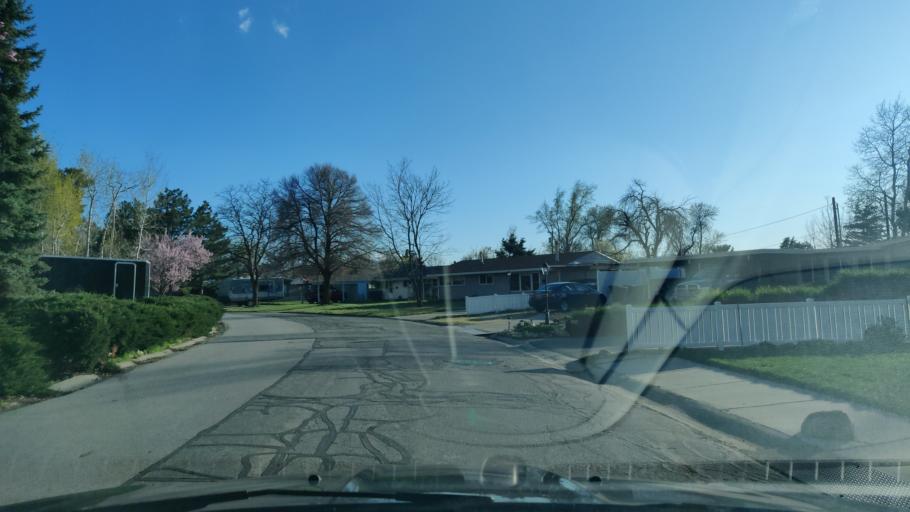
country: US
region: Utah
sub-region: Salt Lake County
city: Cottonwood Heights
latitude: 40.6231
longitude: -111.8095
